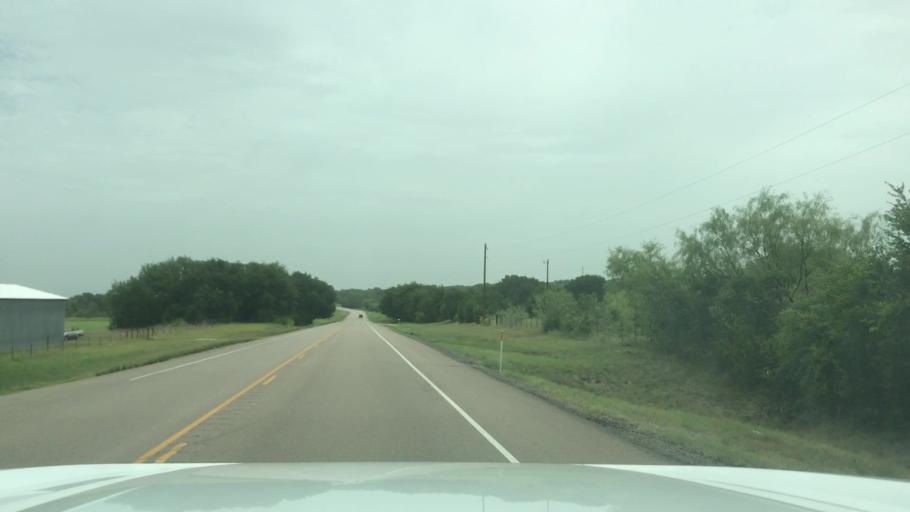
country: US
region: Texas
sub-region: Hamilton County
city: Hico
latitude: 31.9774
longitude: -97.8901
